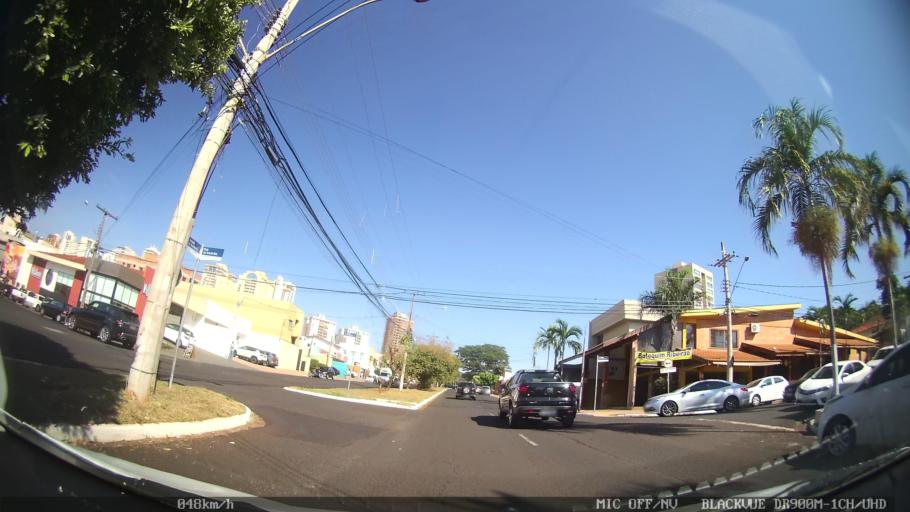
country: BR
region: Sao Paulo
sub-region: Ribeirao Preto
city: Ribeirao Preto
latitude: -21.2017
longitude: -47.8056
